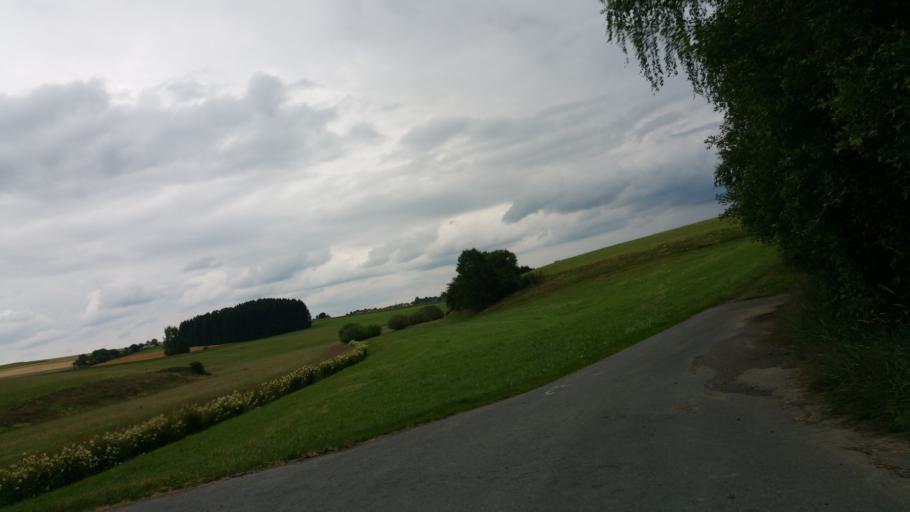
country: DE
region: Bavaria
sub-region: Upper Franconia
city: Oberkotzau
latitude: 50.2454
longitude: 11.9139
